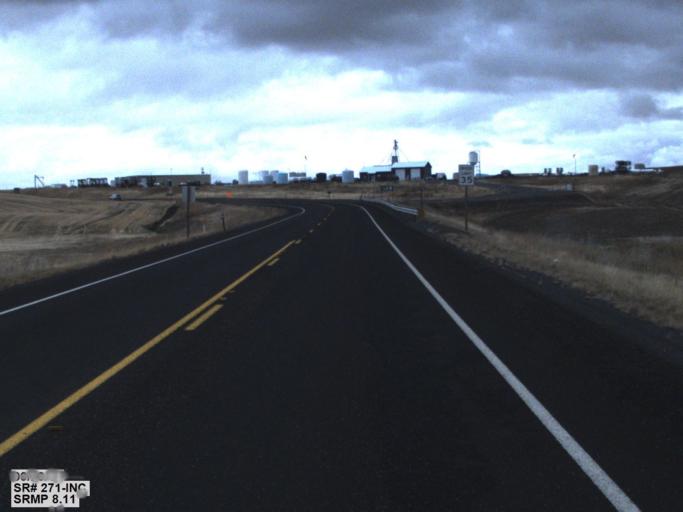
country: US
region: Washington
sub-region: Whitman County
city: Colfax
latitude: 47.2068
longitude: -117.3571
